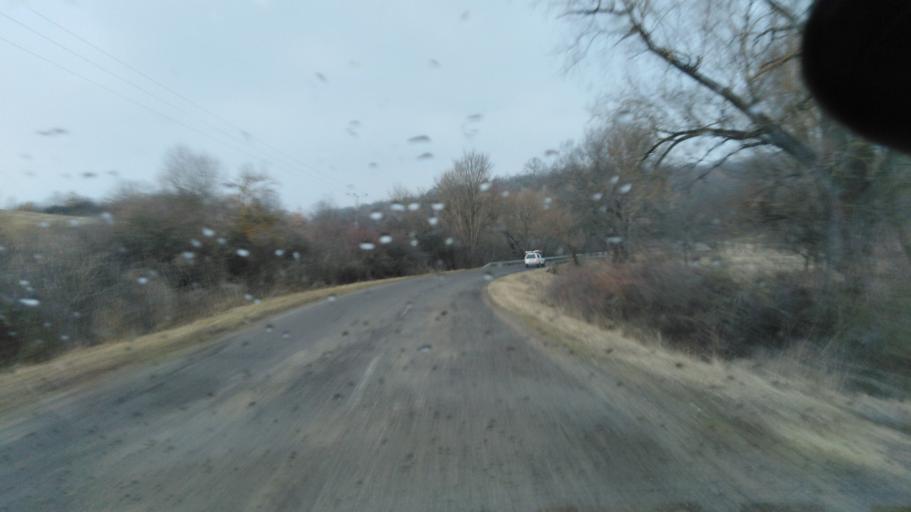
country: HU
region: Nograd
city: Salgotarjan
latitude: 48.0479
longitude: 19.7527
